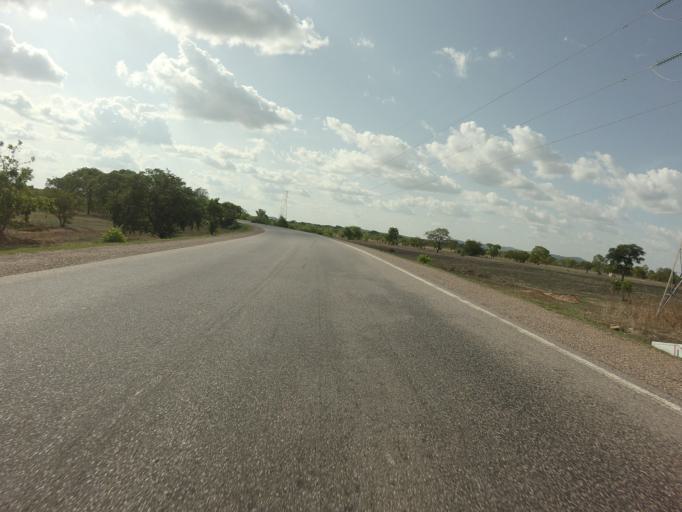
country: GH
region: Upper East
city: Bolgatanga
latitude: 10.5814
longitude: -0.8323
